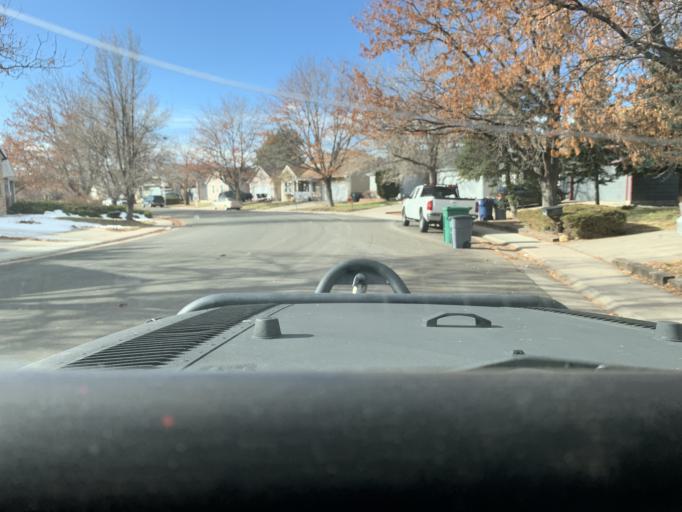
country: US
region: Colorado
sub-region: Adams County
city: Aurora
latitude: 39.7043
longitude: -104.7985
